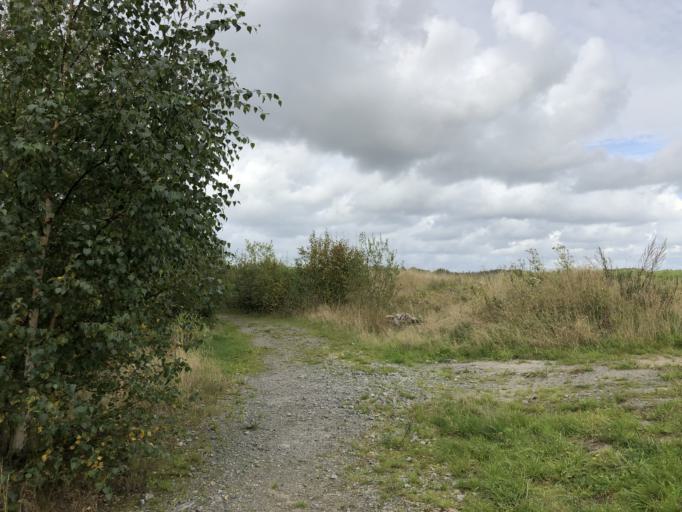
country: SE
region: Vaestra Goetaland
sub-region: Goteborg
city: Majorna
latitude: 57.7632
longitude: 11.8741
